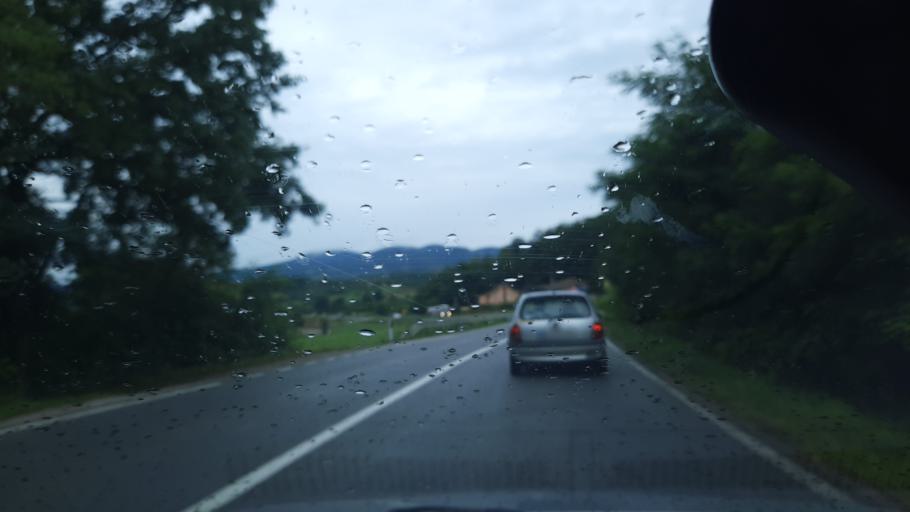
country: RS
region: Central Serbia
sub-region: Sumadijski Okrug
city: Knic
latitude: 43.8577
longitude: 20.7770
